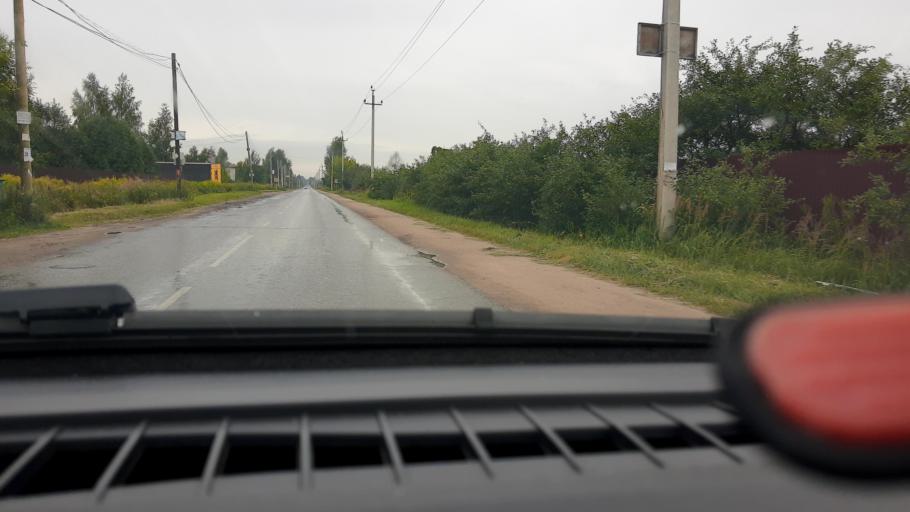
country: RU
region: Nizjnij Novgorod
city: Bor
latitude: 56.3522
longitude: 44.1250
